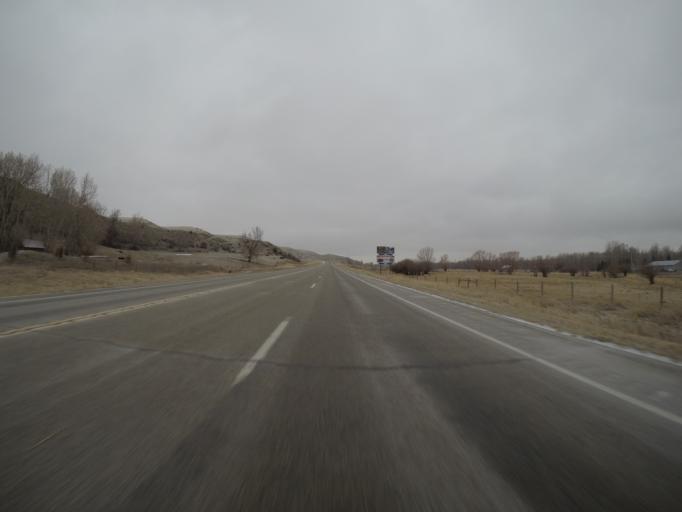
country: US
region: Montana
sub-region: Stillwater County
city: Absarokee
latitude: 45.5057
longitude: -109.4487
